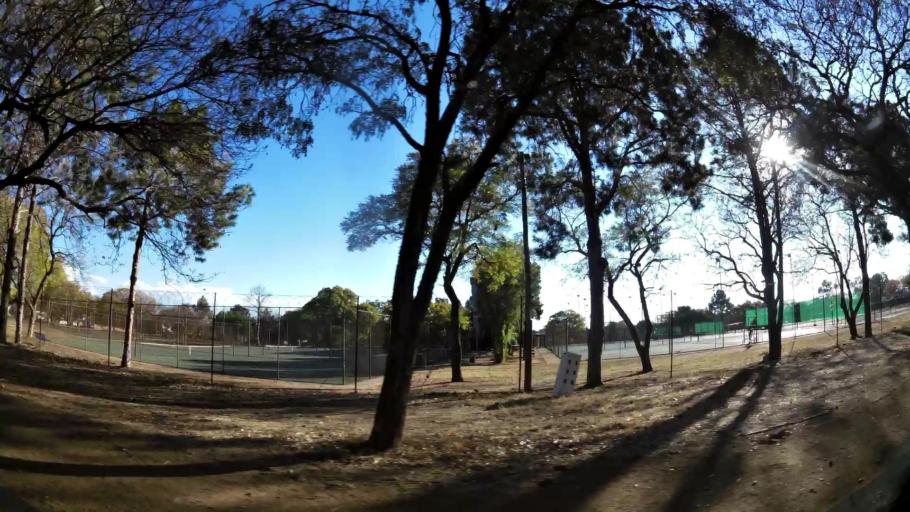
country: ZA
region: Limpopo
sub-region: Capricorn District Municipality
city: Polokwane
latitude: -23.9017
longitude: 29.4617
